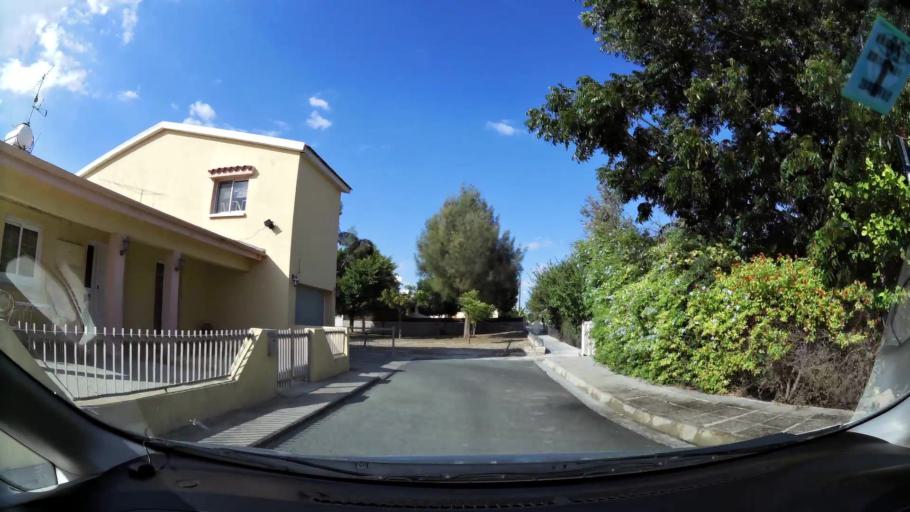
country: CY
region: Larnaka
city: Livadia
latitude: 34.9474
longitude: 33.6217
